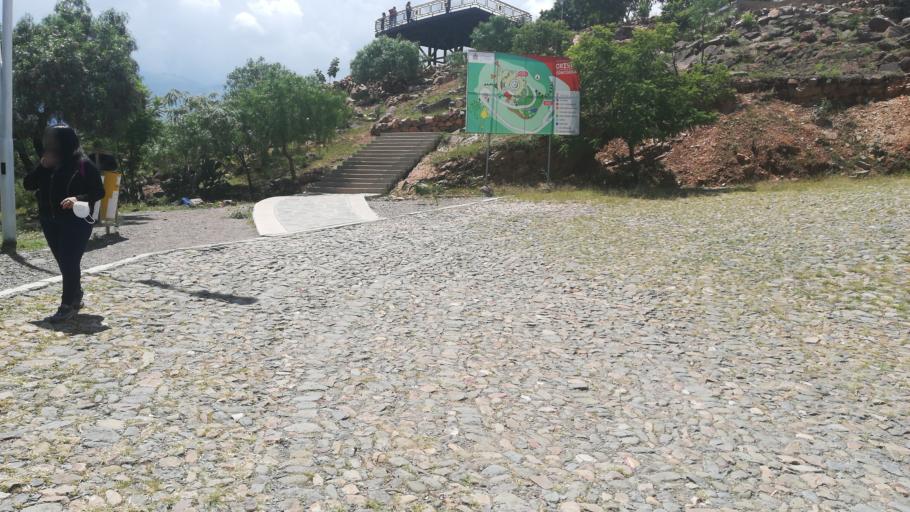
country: BO
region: Cochabamba
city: Cochabamba
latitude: -17.3846
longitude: -66.1358
